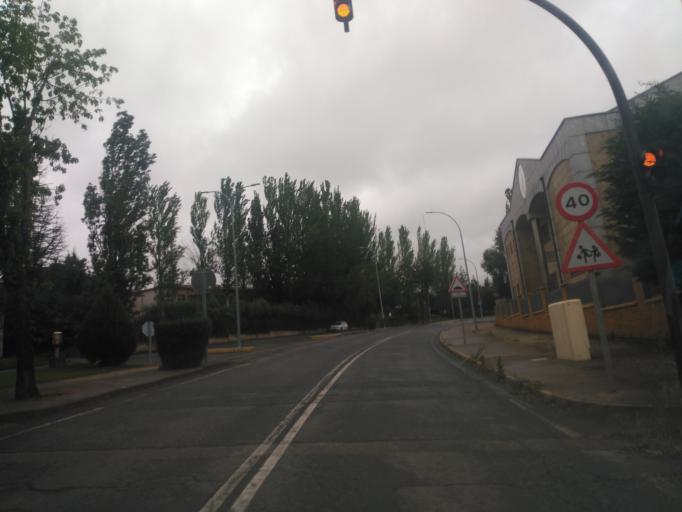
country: ES
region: Castille and Leon
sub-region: Provincia de Salamanca
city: Guijuelo
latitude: 40.5468
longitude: -5.6765
